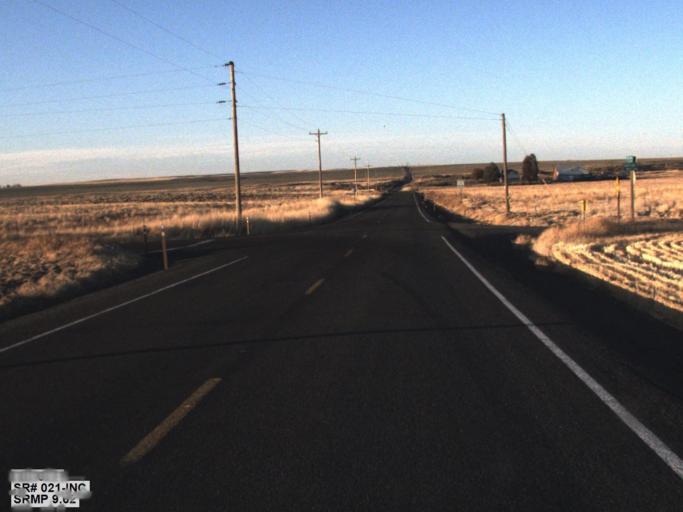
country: US
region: Washington
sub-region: Franklin County
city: Connell
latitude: 46.7655
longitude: -118.5476
